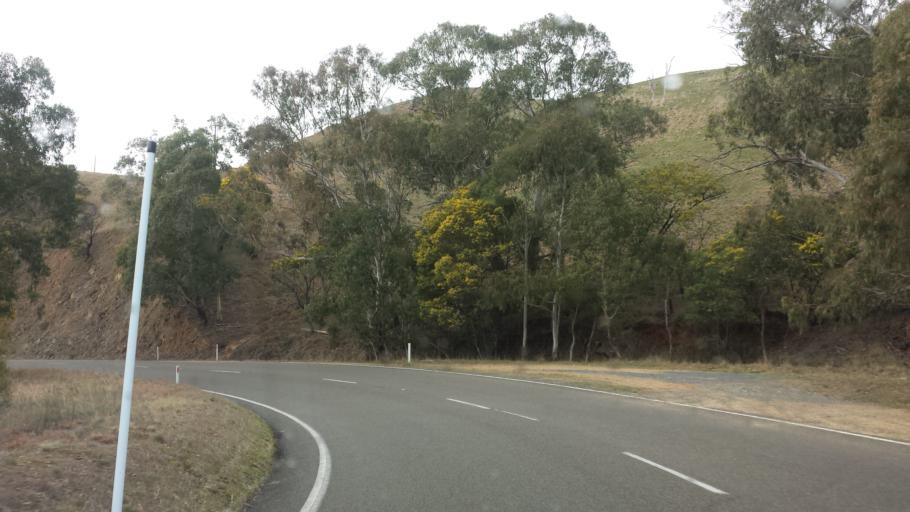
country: AU
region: Victoria
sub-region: Alpine
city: Mount Beauty
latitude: -37.1149
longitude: 147.5609
